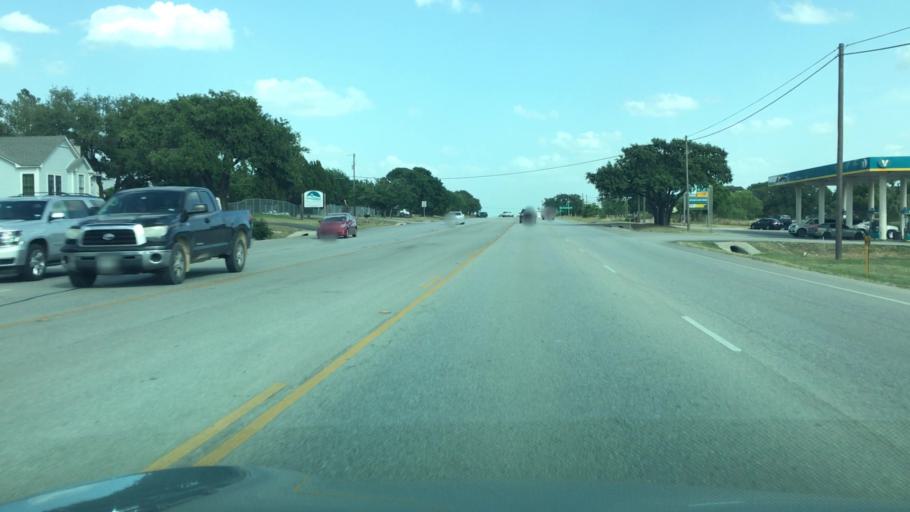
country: US
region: Texas
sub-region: Hays County
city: Dripping Springs
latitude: 30.1986
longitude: -98.1075
